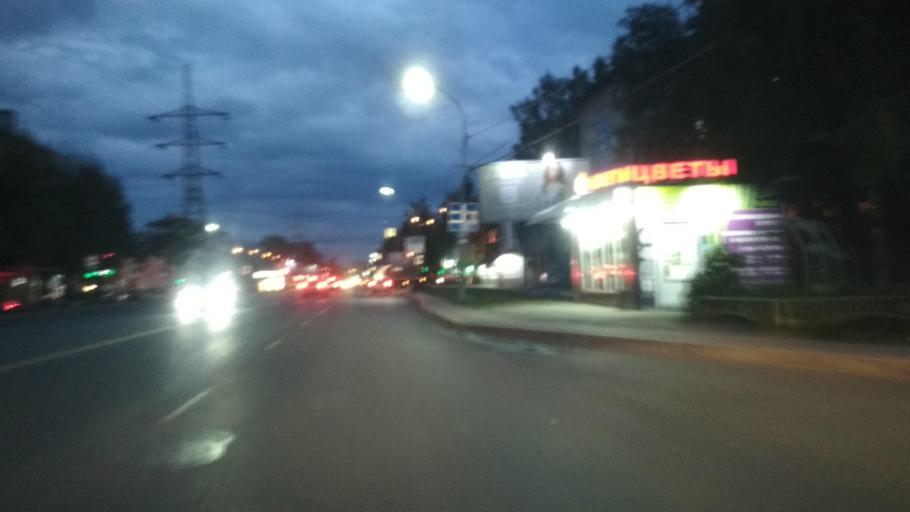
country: RU
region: Tomsk
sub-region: Tomskiy Rayon
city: Tomsk
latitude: 56.4629
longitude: 84.9900
